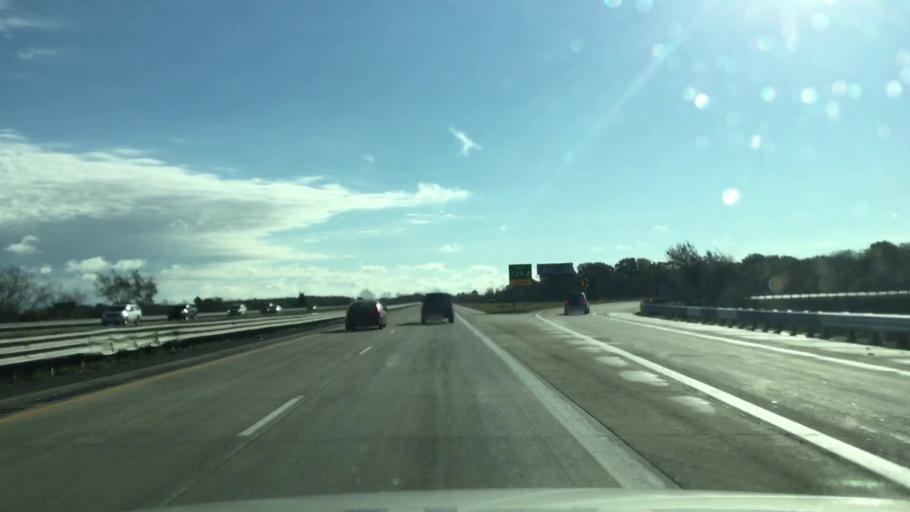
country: US
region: Michigan
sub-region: Genesee County
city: Swartz Creek
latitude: 42.9656
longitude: -83.8065
